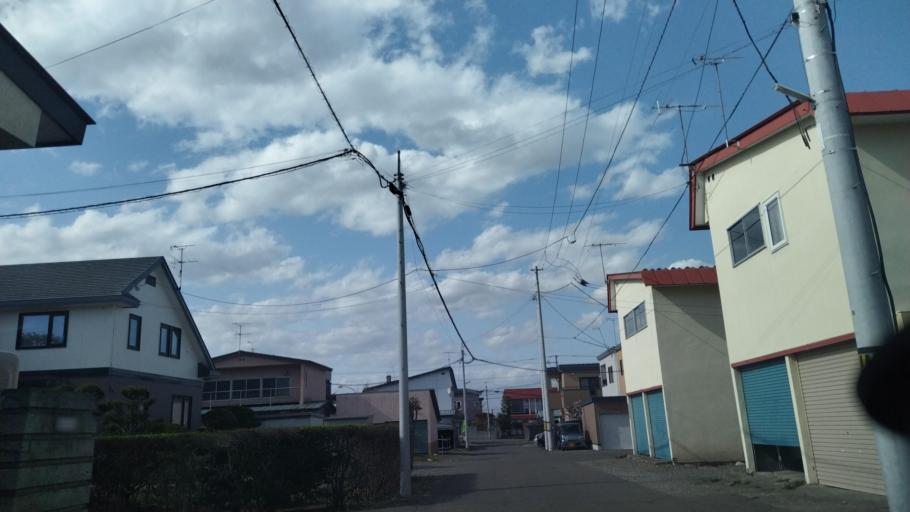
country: JP
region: Hokkaido
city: Obihiro
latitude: 42.9310
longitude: 143.1677
